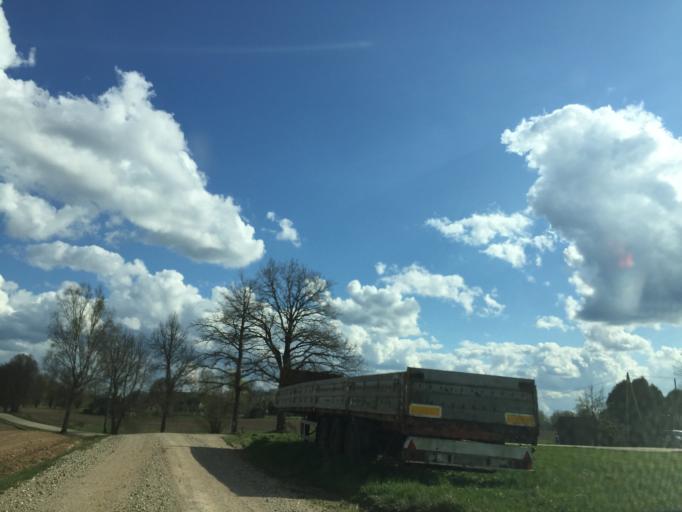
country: LV
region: Beverina
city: Murmuiza
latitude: 57.4216
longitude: 25.5497
